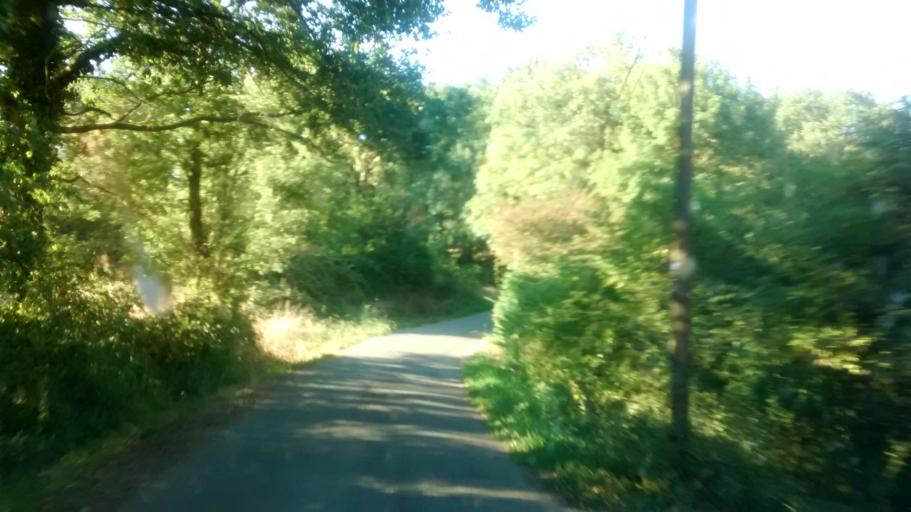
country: FR
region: Midi-Pyrenees
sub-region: Departement de la Haute-Garonne
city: Lherm
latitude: 43.4211
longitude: 1.2182
